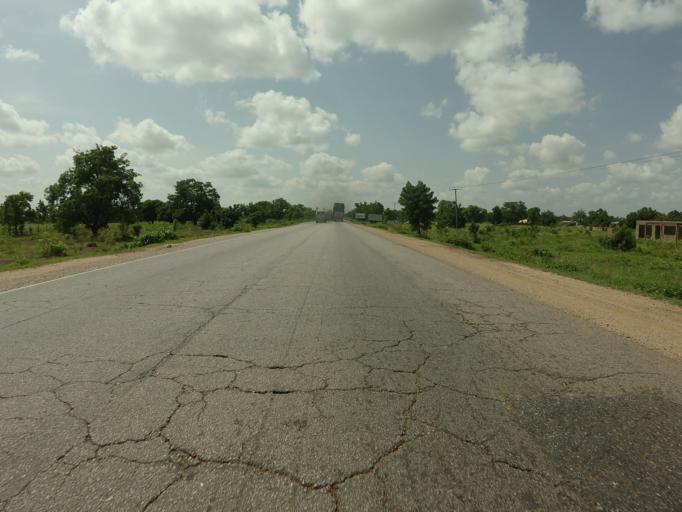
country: GH
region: Northern
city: Savelugu
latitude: 9.5607
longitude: -0.8364
